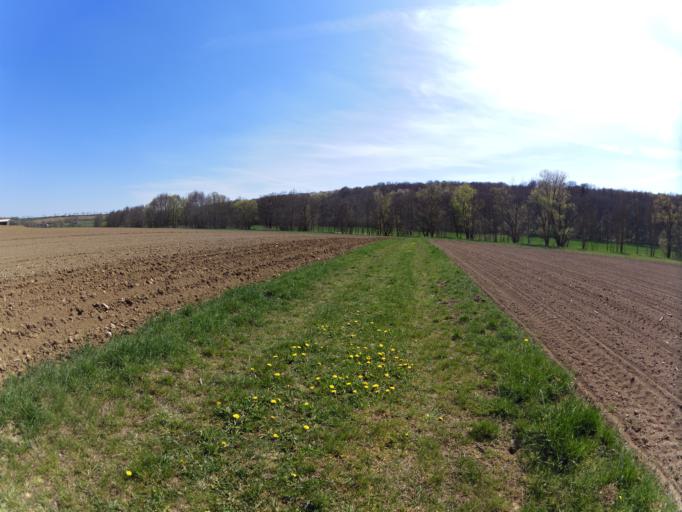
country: DE
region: Bavaria
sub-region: Regierungsbezirk Unterfranken
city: Estenfeld
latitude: 49.8585
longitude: 9.9997
